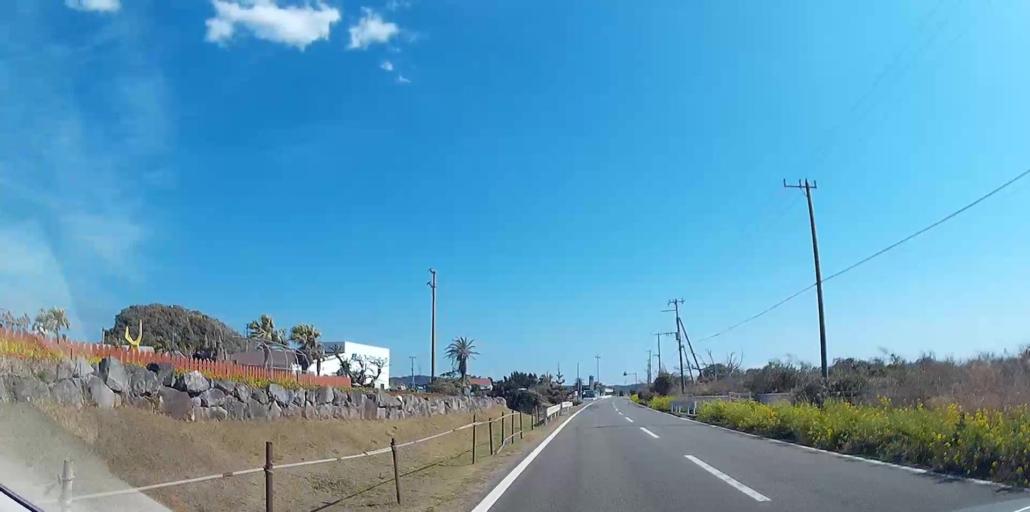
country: JP
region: Chiba
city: Tateyama
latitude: 34.9466
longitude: 139.8128
